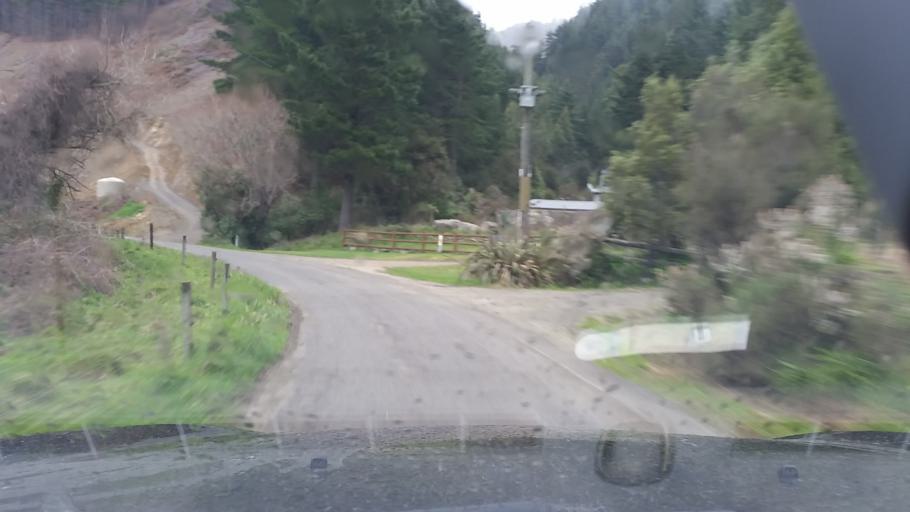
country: NZ
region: Marlborough
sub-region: Marlborough District
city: Blenheim
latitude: -41.4009
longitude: 173.8481
